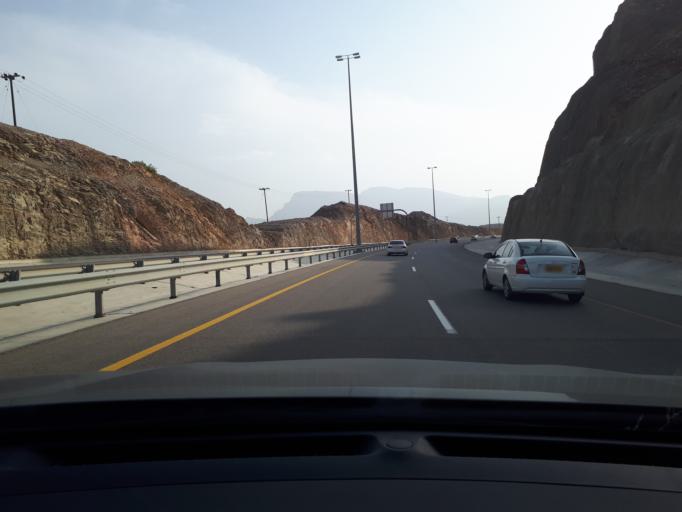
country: OM
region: Muhafazat Masqat
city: Muscat
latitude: 23.1931
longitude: 58.8780
